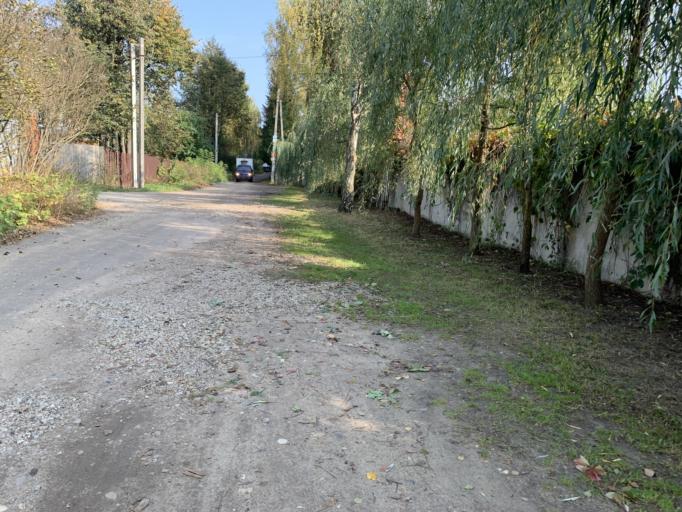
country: RU
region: Moskovskaya
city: Mamontovka
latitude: 55.9648
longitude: 37.8291
